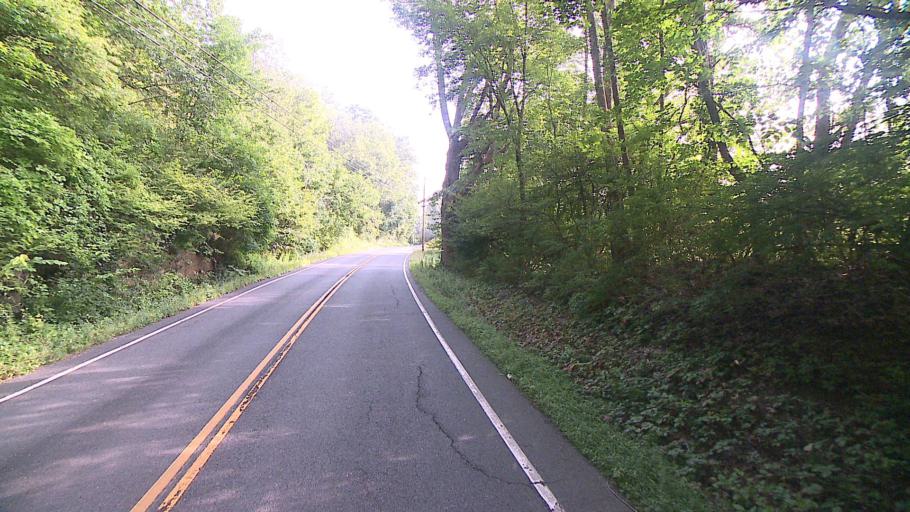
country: US
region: Connecticut
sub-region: Litchfield County
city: Canaan
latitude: 41.9248
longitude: -73.3627
